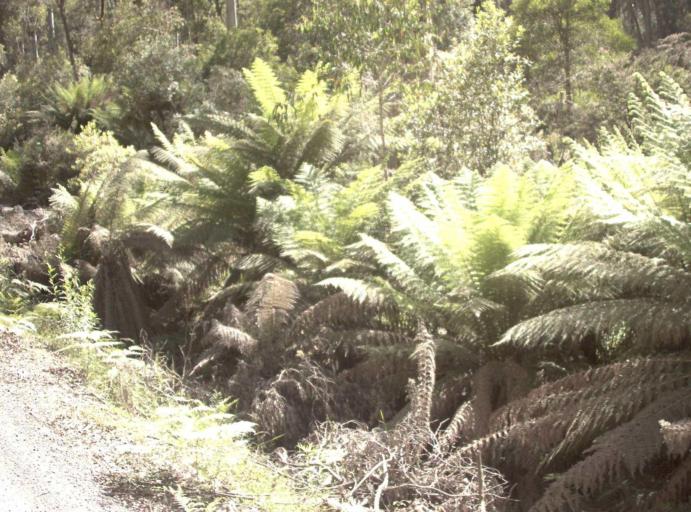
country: AU
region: New South Wales
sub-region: Bombala
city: Bombala
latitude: -37.2168
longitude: 148.7464
